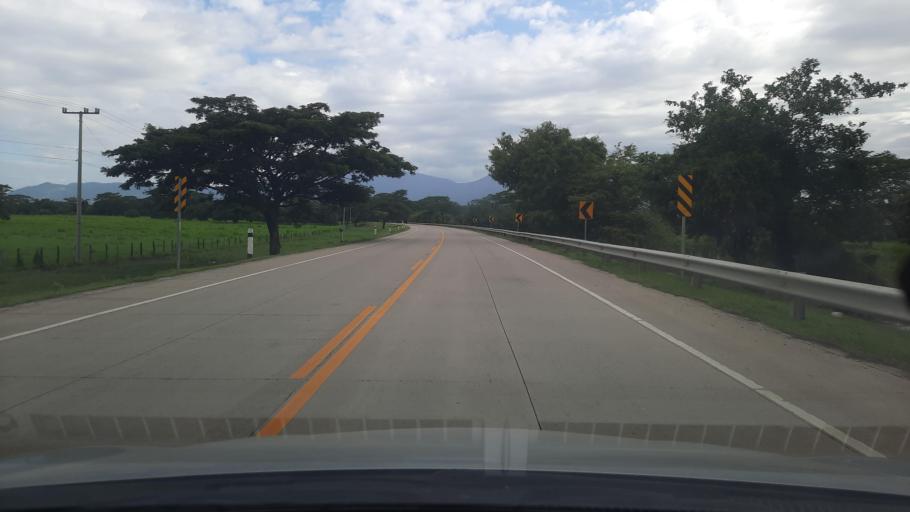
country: NI
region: Chinandega
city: Somotillo
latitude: 12.8327
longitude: -86.8948
